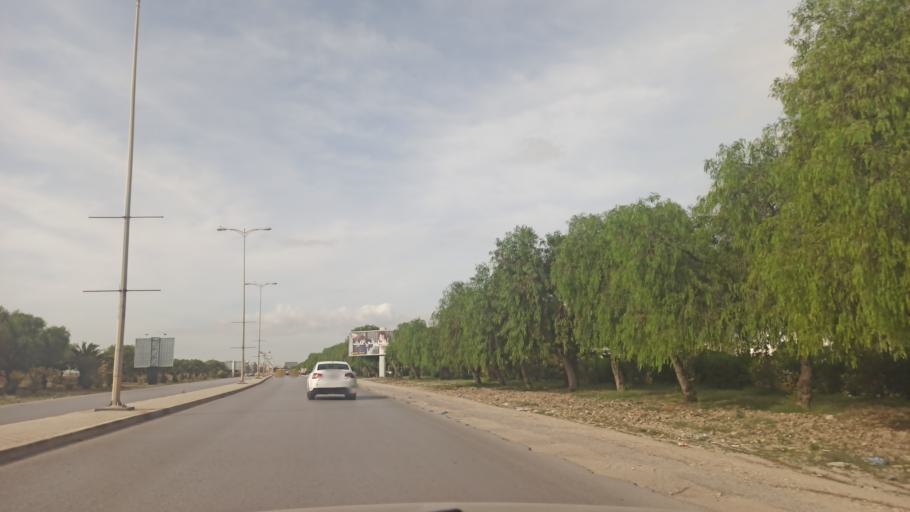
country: TN
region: Tunis
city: La Goulette
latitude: 36.8449
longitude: 10.2566
